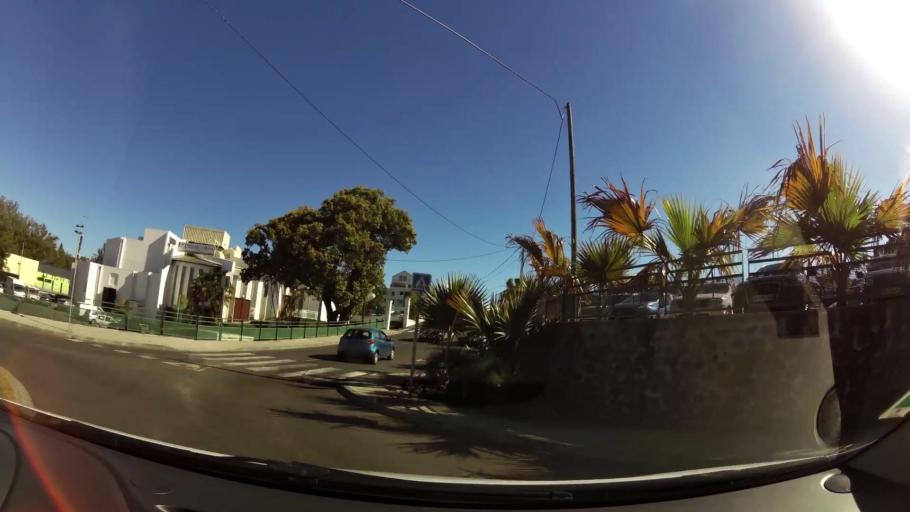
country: RE
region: Reunion
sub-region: Reunion
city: Le Tampon
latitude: -21.2805
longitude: 55.5208
